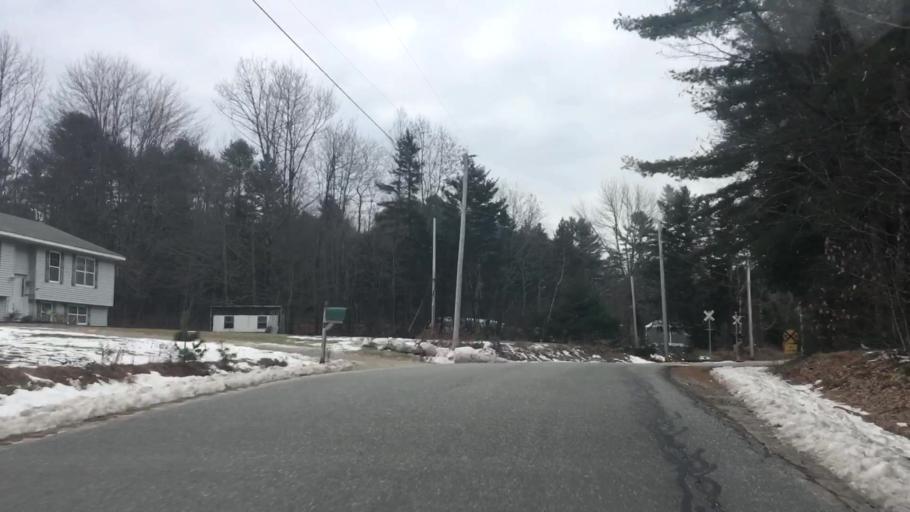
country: US
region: Maine
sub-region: Cumberland County
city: Freeport
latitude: 43.8703
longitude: -70.0912
